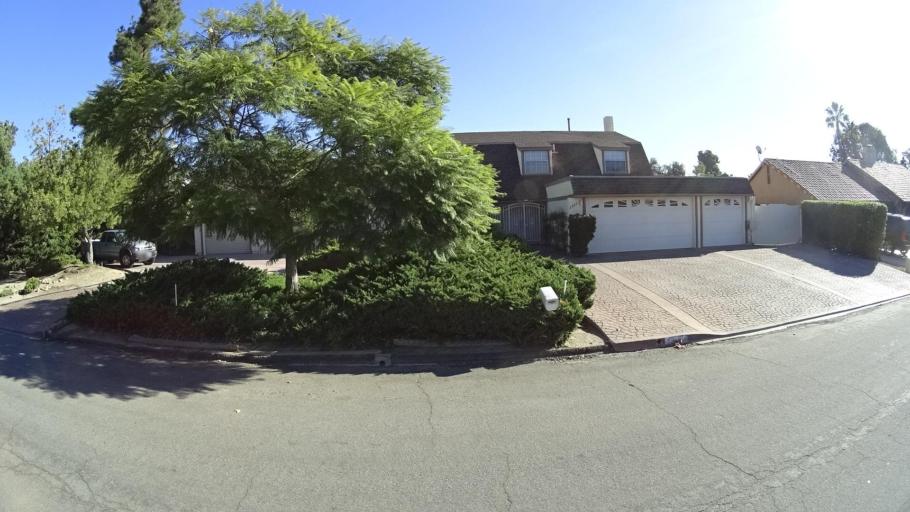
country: US
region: California
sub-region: San Diego County
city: Bonita
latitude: 32.6826
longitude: -117.0253
